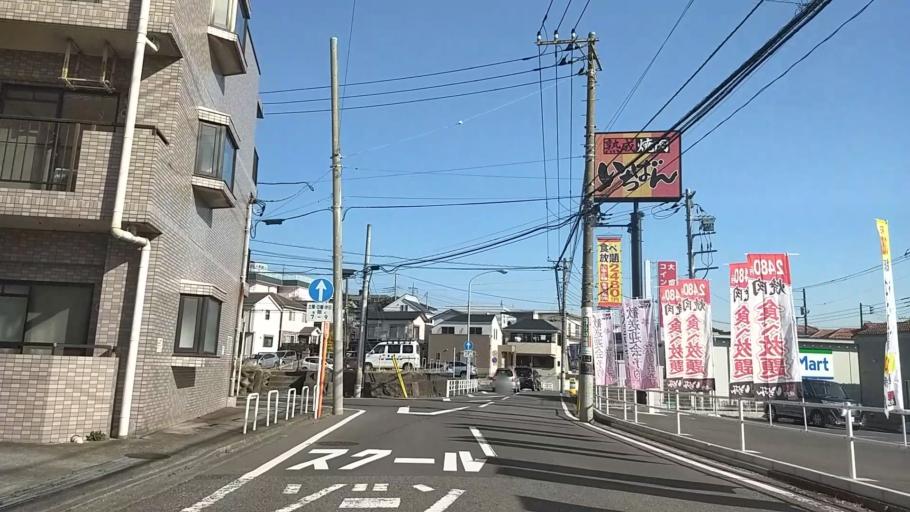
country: JP
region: Kanagawa
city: Yokohama
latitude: 35.3883
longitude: 139.5960
